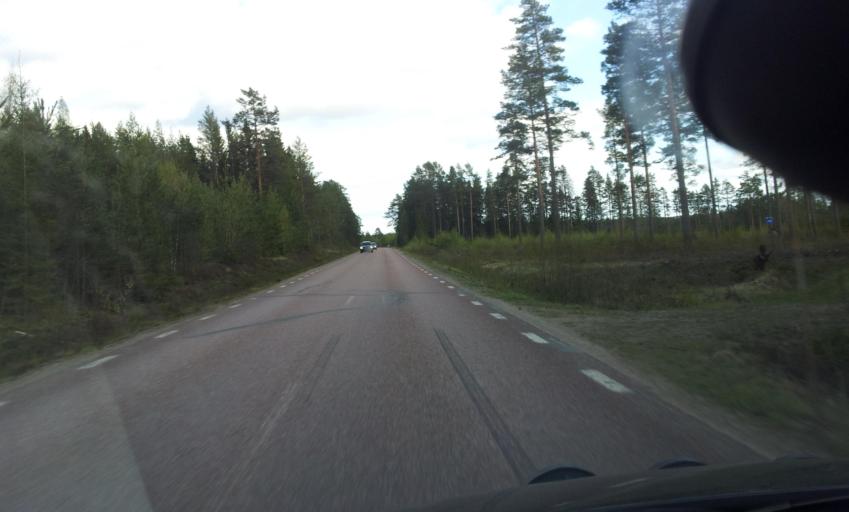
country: SE
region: Gaevleborg
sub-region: Bollnas Kommun
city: Kilafors
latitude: 61.3864
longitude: 16.6110
